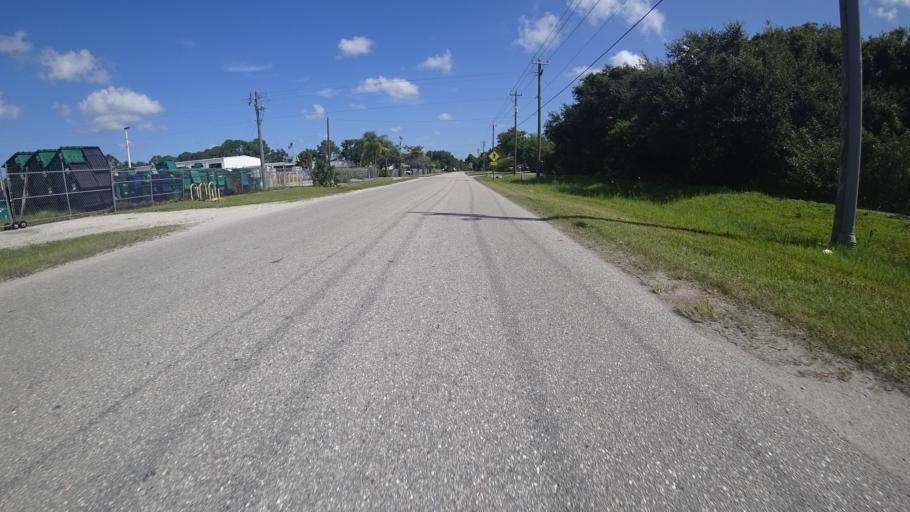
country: US
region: Florida
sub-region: Manatee County
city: Whitfield
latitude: 27.4307
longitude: -82.5384
